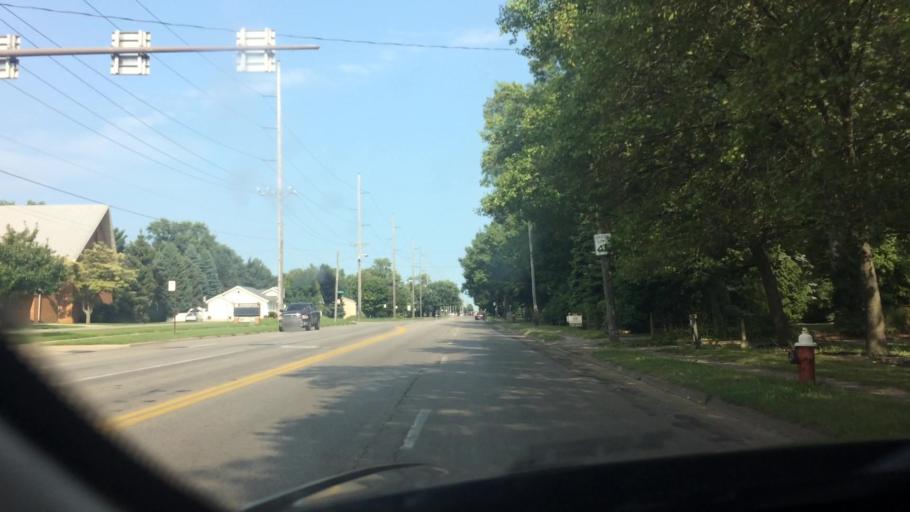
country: US
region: Ohio
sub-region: Lucas County
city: Ottawa Hills
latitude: 41.7062
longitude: -83.6227
